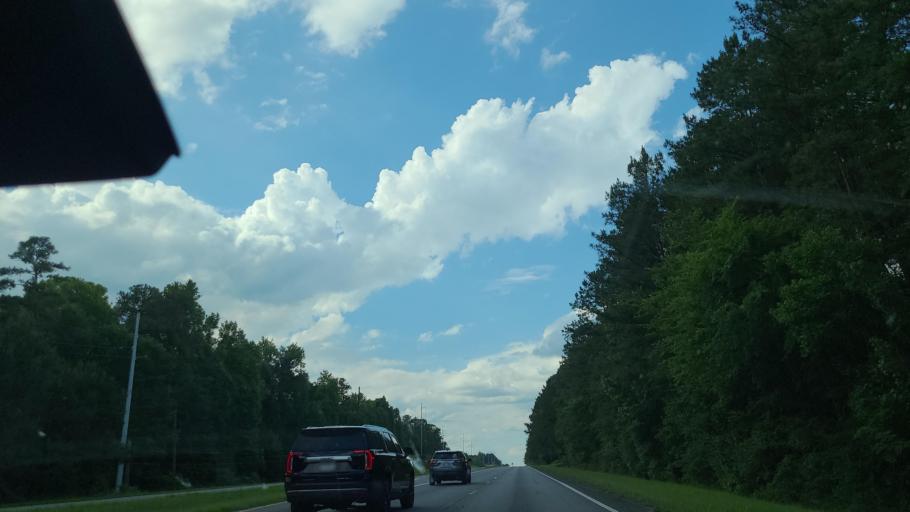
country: US
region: Georgia
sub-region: Jones County
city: Gray
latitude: 32.9535
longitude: -83.5798
